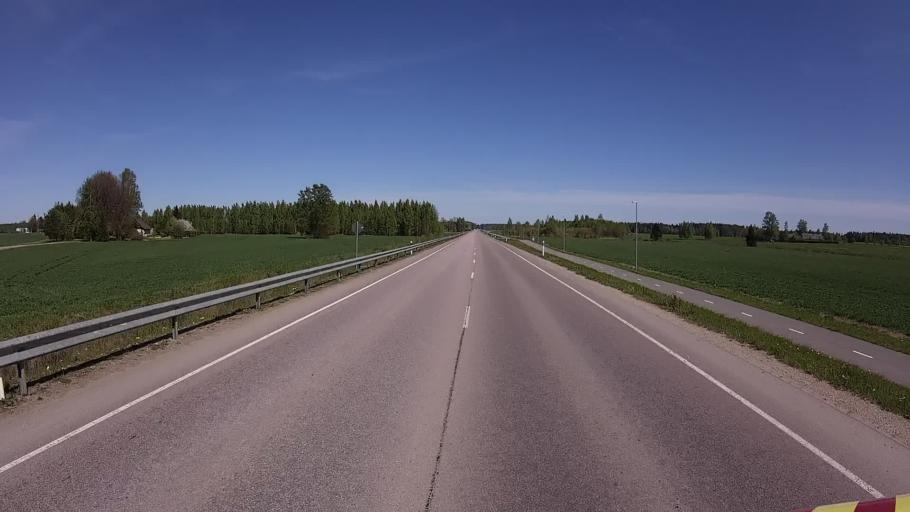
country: EE
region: Polvamaa
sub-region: Polva linn
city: Polva
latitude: 58.0739
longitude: 27.0880
